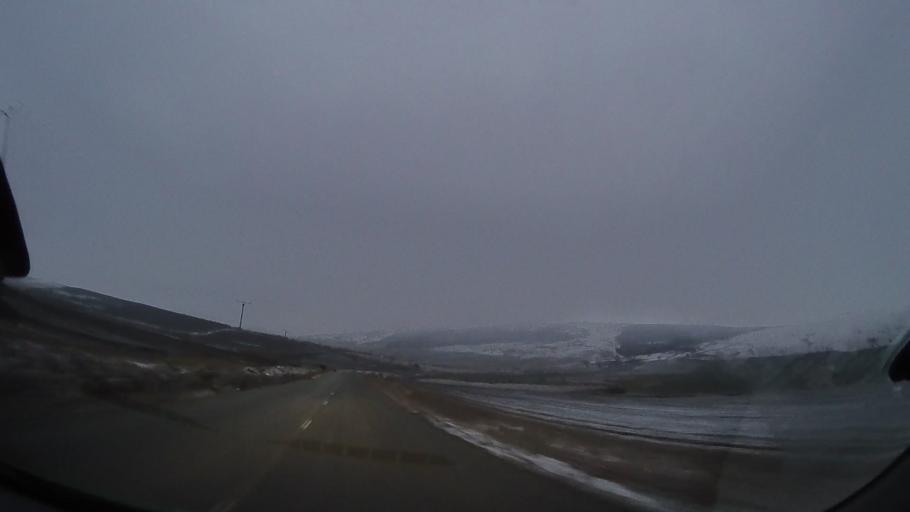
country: RO
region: Vaslui
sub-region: Comuna Vutcani
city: Vutcani
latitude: 46.4016
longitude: 27.9851
